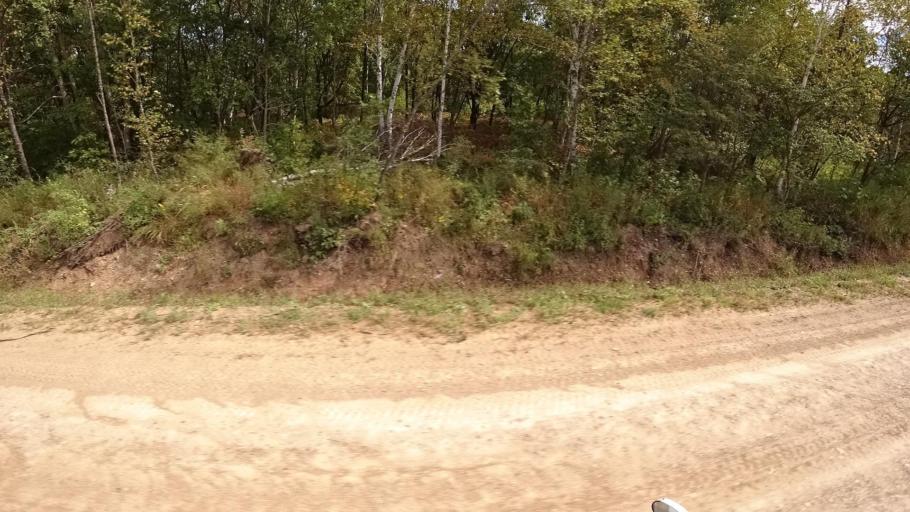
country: RU
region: Primorskiy
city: Yakovlevka
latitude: 44.7341
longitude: 133.6085
